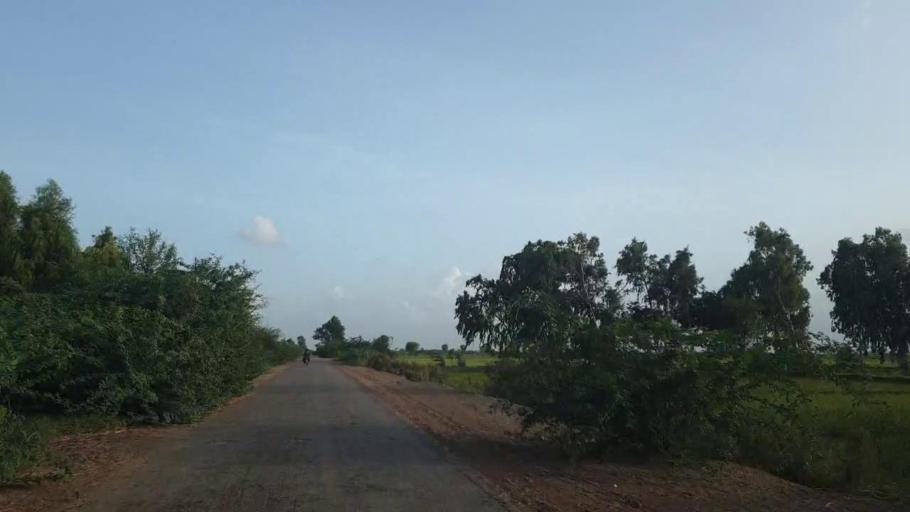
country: PK
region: Sindh
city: Kadhan
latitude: 24.6140
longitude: 69.1158
